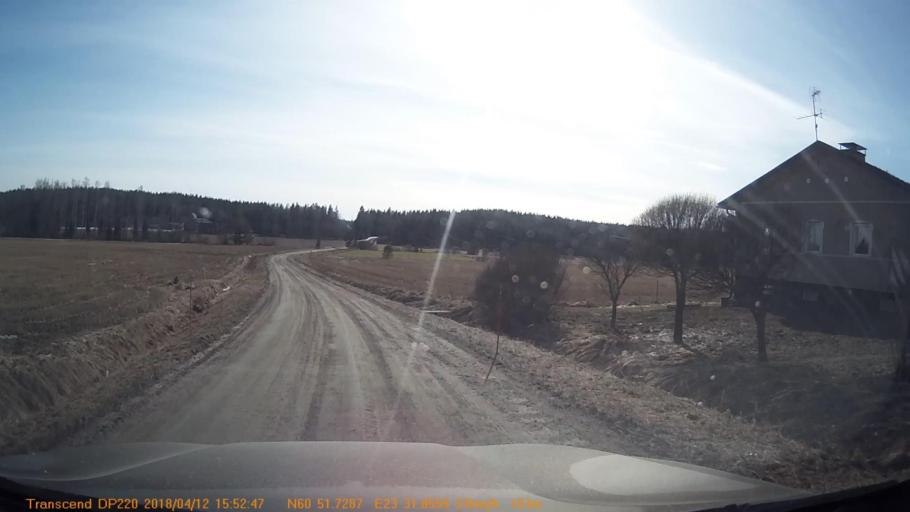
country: FI
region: Haeme
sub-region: Forssa
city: Jokioinen
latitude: 60.8621
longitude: 23.5309
